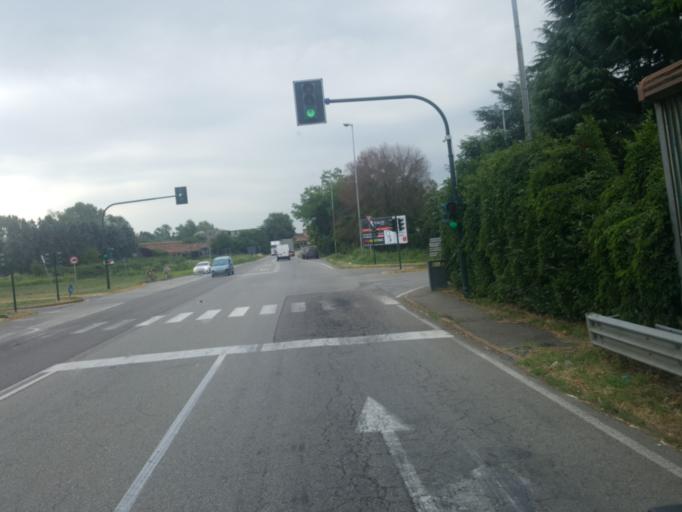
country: IT
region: Lombardy
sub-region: Citta metropolitana di Milano
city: Melzo
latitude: 45.4930
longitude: 9.4218
